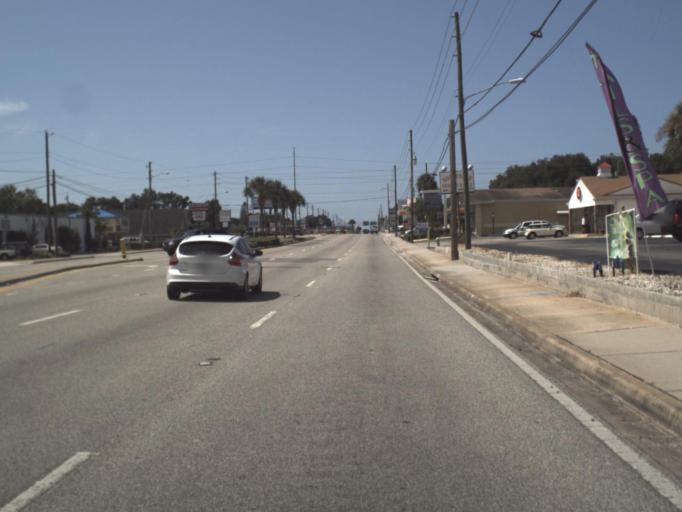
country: US
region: Florida
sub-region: Pinellas County
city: Seminole
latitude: 27.8320
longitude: -82.7872
